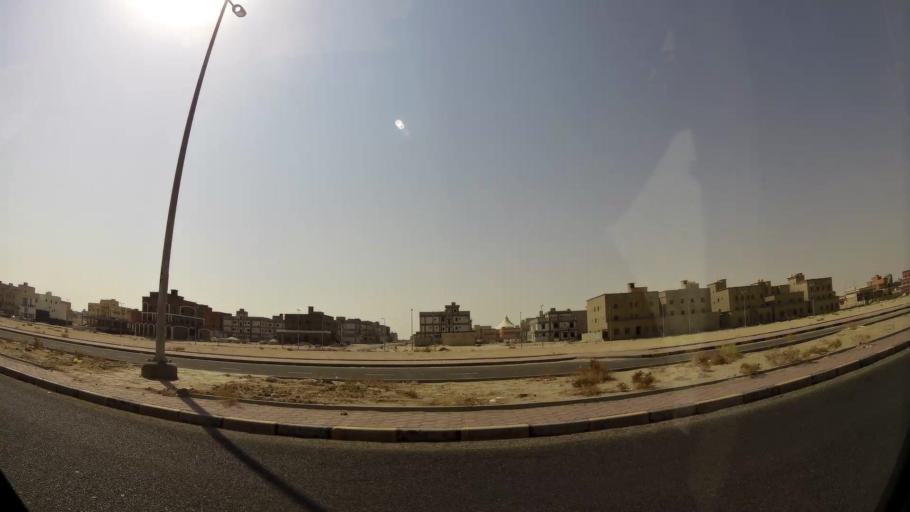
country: KW
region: Al Ahmadi
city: Al Wafrah
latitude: 28.7995
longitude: 48.0565
